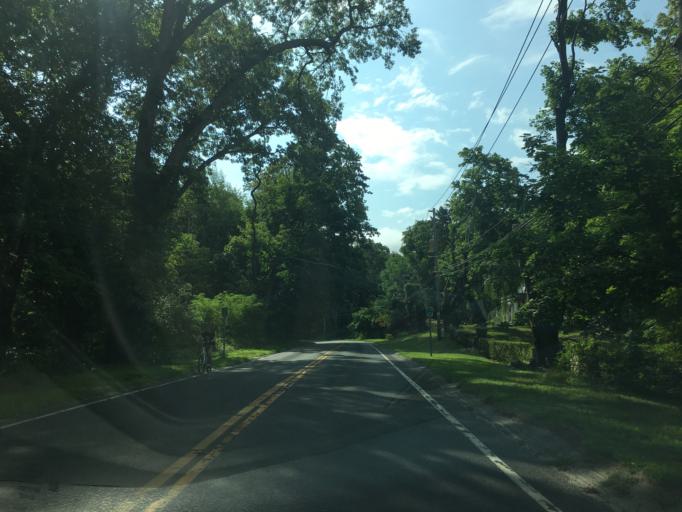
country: US
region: New York
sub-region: Suffolk County
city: Shelter Island
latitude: 41.0759
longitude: -72.3457
